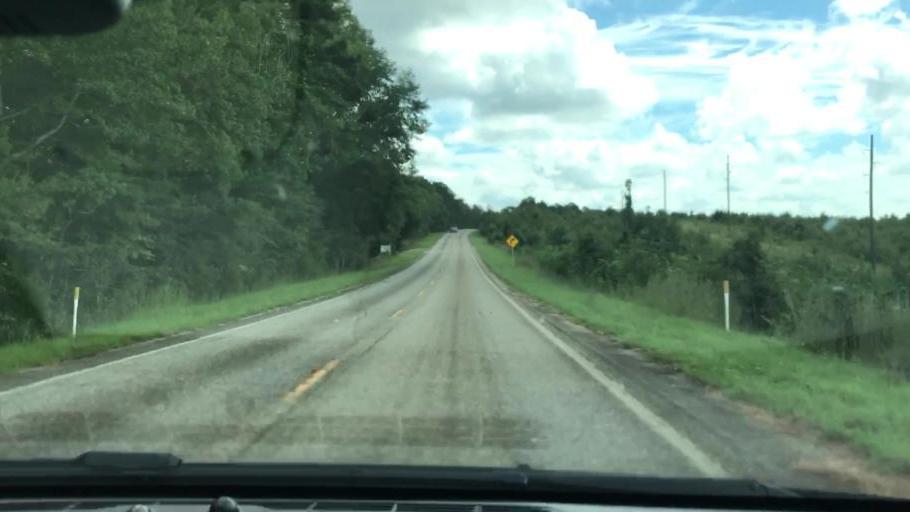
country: US
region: Georgia
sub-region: Stewart County
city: Lumpkin
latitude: 32.0720
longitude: -84.8487
